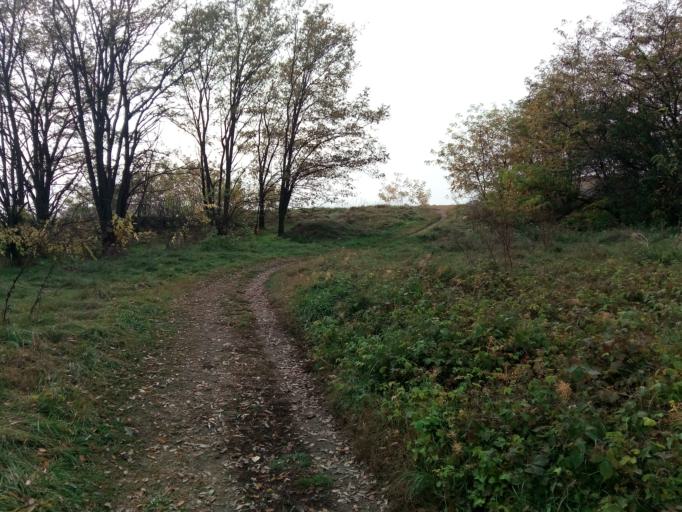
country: HU
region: Pest
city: Vecses
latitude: 47.4207
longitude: 19.2886
